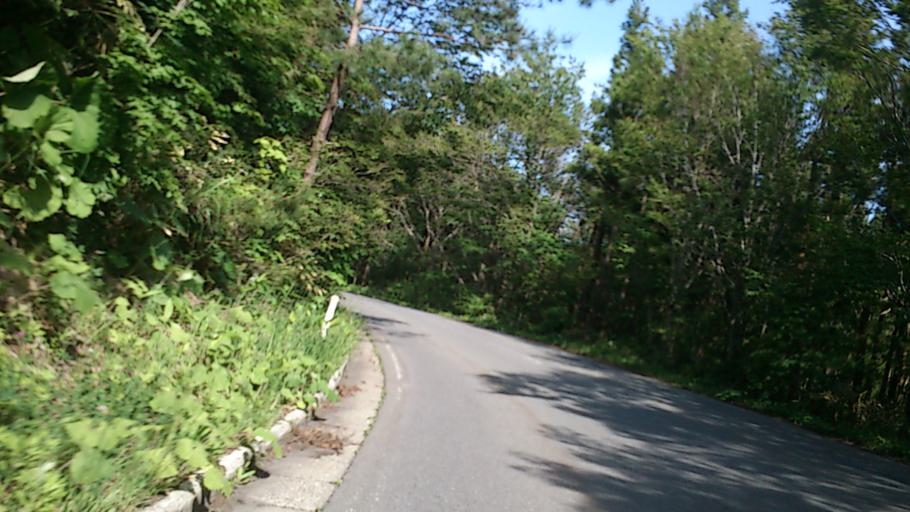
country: JP
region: Aomori
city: Aomori Shi
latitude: 40.7181
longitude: 140.8095
